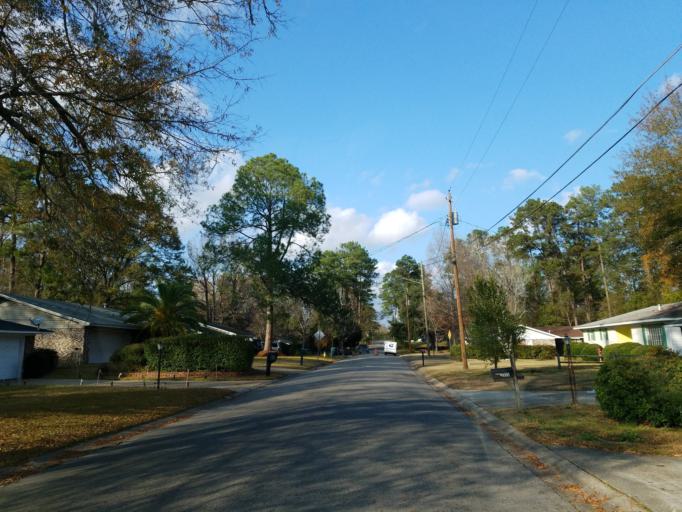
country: US
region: Mississippi
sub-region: Forrest County
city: Hattiesburg
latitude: 31.3297
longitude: -89.3222
